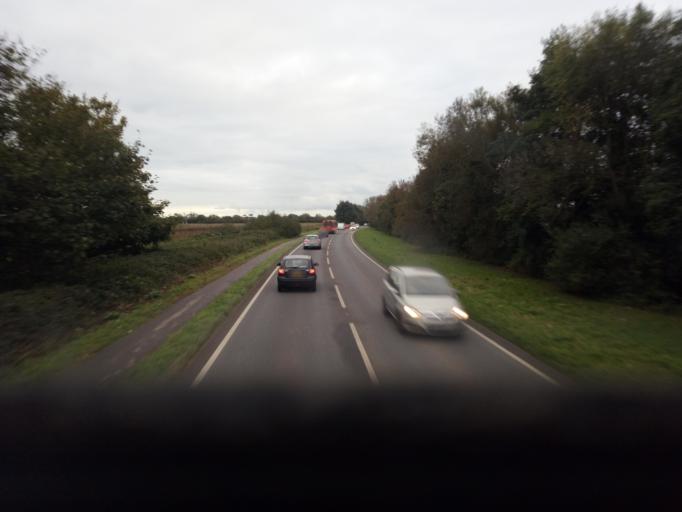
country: GB
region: England
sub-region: West Sussex
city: Boxgrove
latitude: 50.8188
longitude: -0.7150
